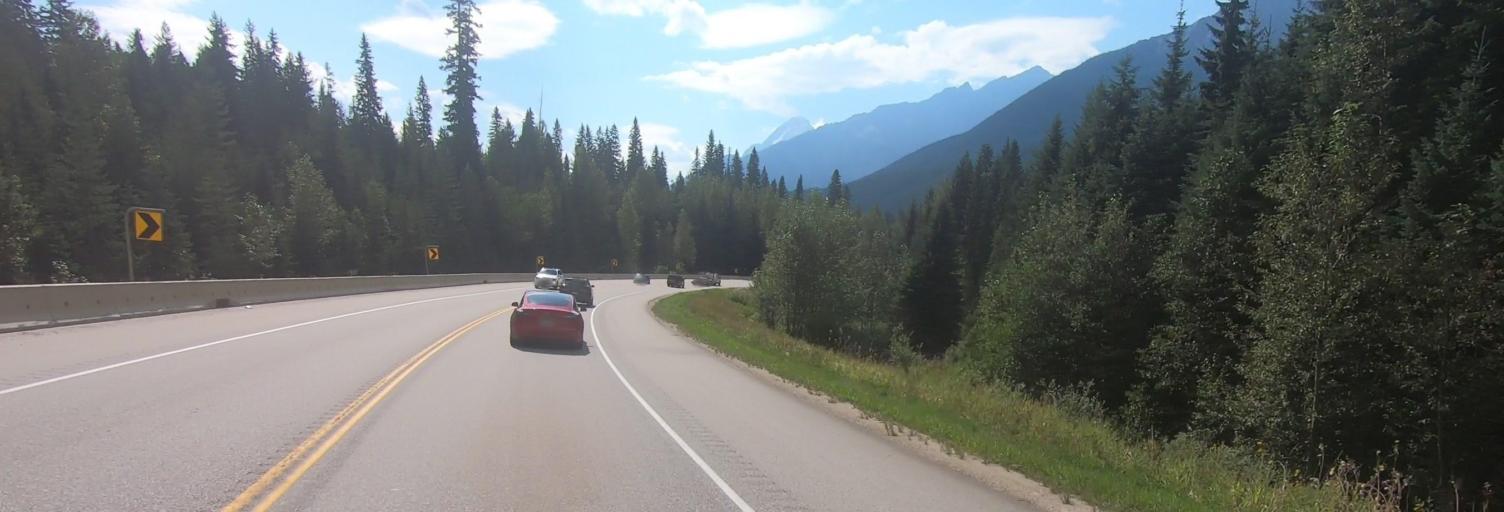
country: CA
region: British Columbia
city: Golden
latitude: 51.3871
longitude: -117.4485
